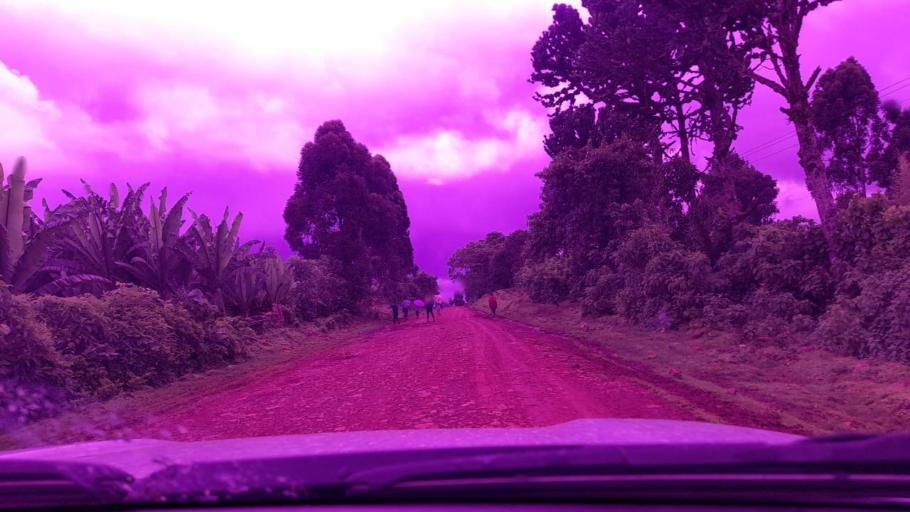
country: ET
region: Southern Nations, Nationalities, and People's Region
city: Tippi
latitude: 7.5774
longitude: 35.6338
